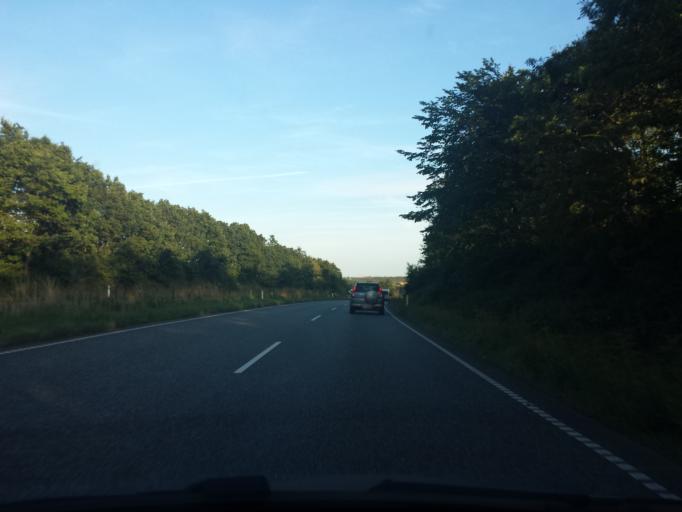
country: DK
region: Capital Region
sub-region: Egedal Kommune
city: Vekso
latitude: 55.7553
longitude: 12.2462
